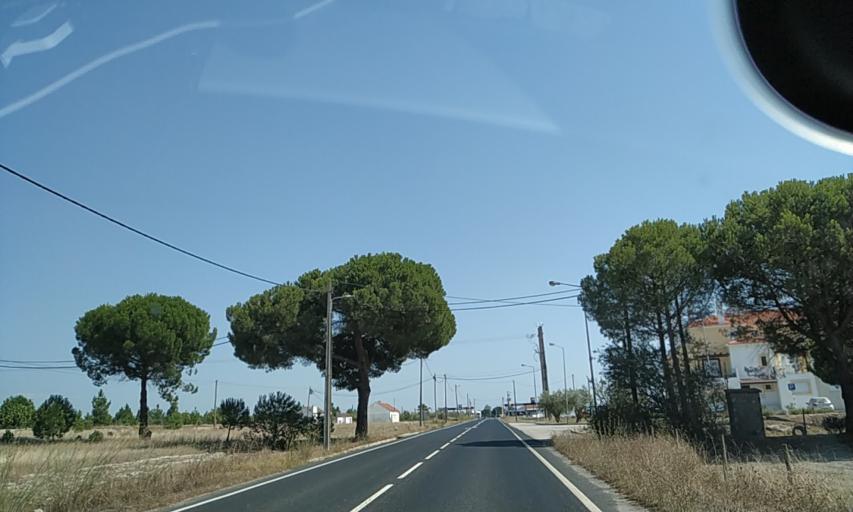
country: PT
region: Santarem
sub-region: Benavente
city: Poceirao
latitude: 38.7462
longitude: -8.6635
